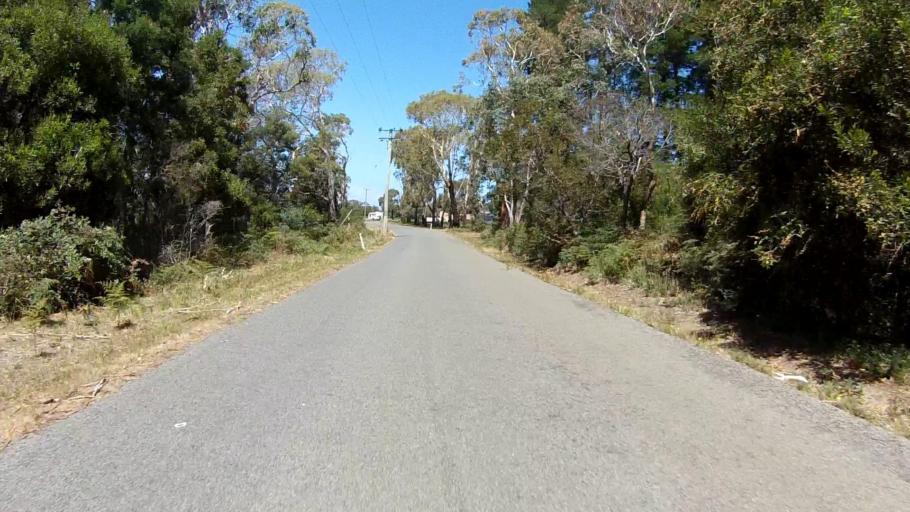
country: AU
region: Tasmania
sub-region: Clarence
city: Sandford
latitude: -42.9326
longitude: 147.4996
